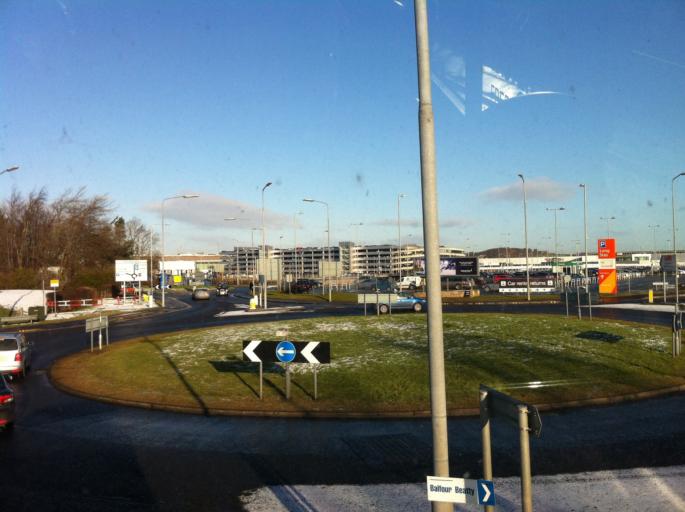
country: GB
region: Scotland
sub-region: Edinburgh
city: Ratho
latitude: 55.9440
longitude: -3.3611
